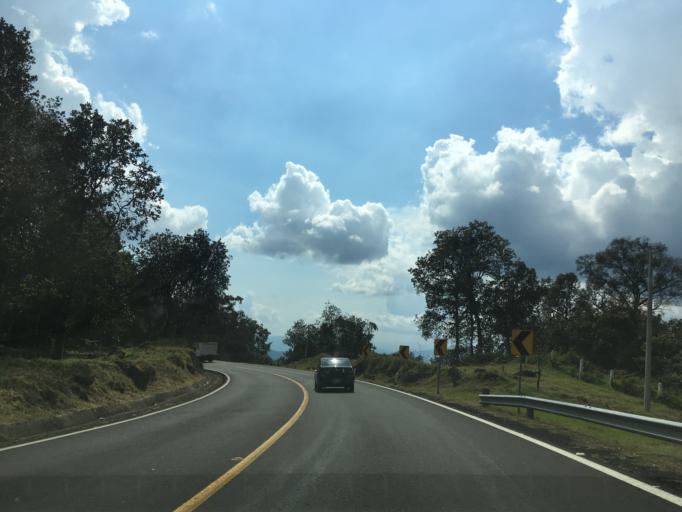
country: MX
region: Michoacan
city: Tingambato
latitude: 19.5103
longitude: -101.8383
